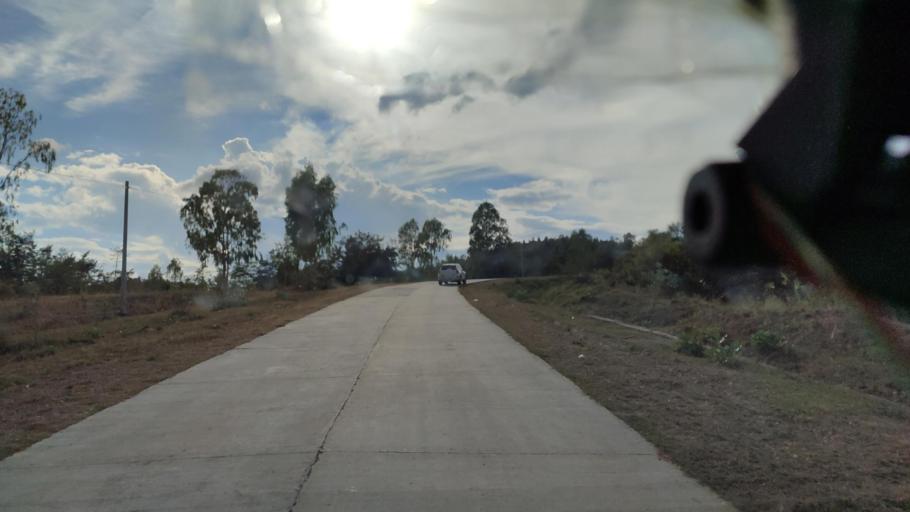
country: MM
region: Mandalay
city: Yamethin
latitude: 20.1319
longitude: 96.0783
